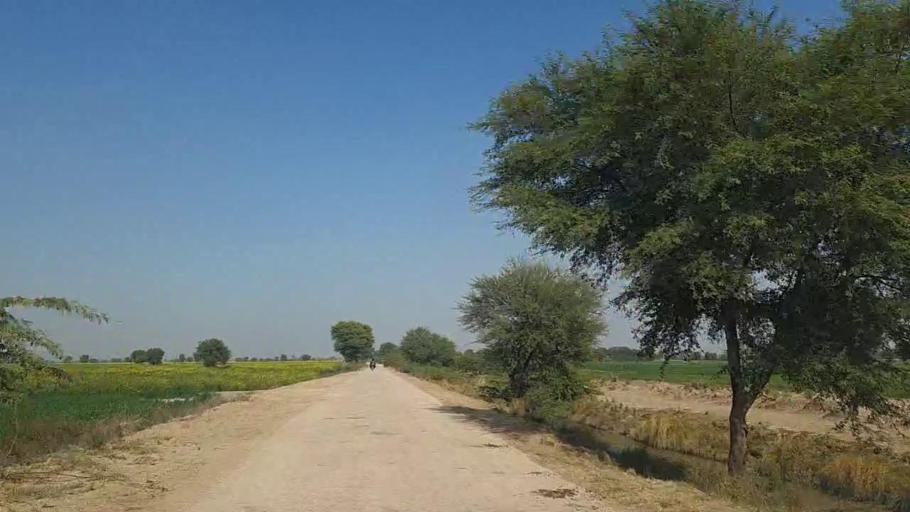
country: PK
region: Sindh
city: Shahpur Chakar
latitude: 26.1861
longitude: 68.6029
